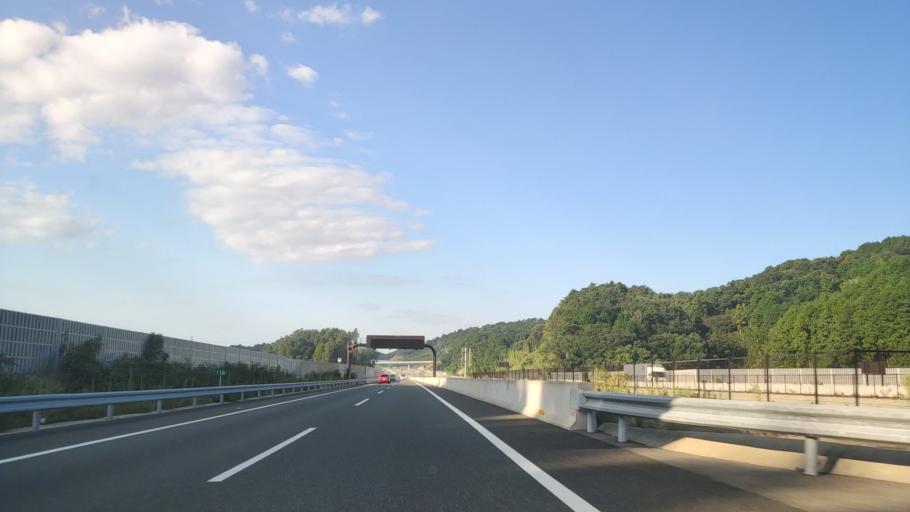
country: JP
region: Osaka
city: Ibaraki
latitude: 34.8903
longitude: 135.5423
